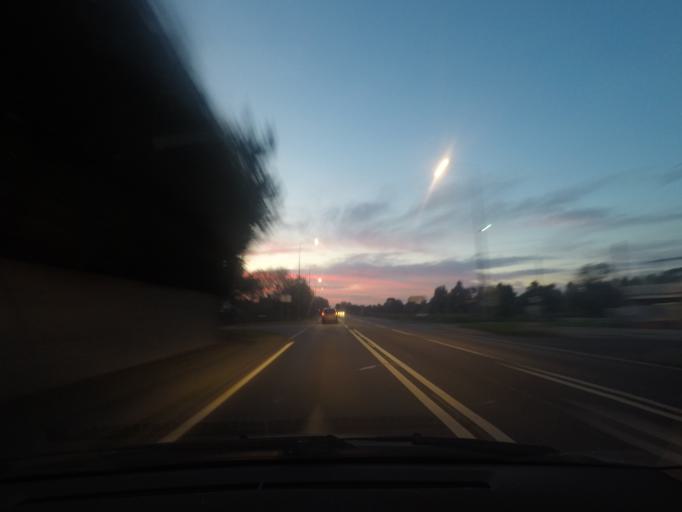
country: GB
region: England
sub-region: East Riding of Yorkshire
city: Thornton
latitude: 53.9330
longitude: -0.8375
